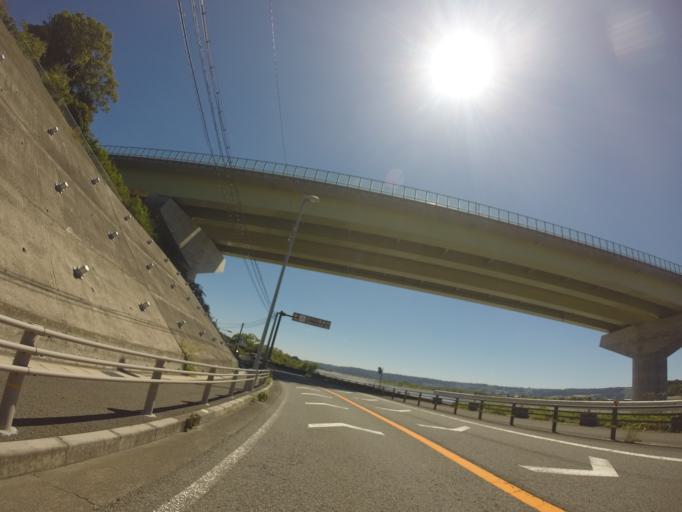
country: JP
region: Shizuoka
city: Kanaya
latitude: 34.8561
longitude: 138.1358
